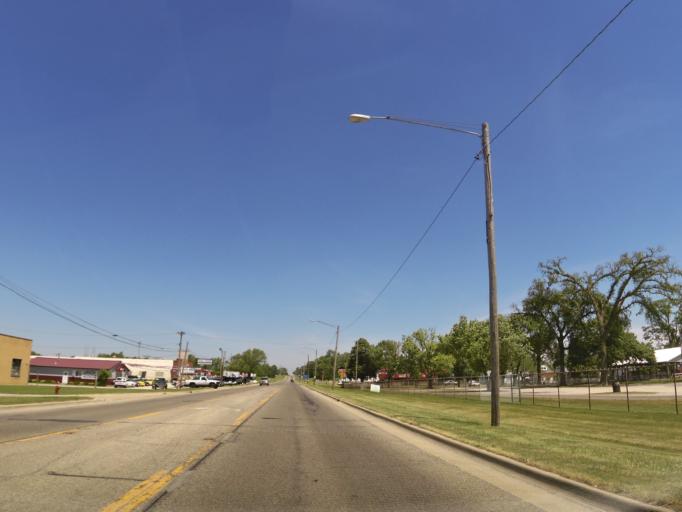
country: US
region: Illinois
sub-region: Vermilion County
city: Hoopeston
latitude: 40.4644
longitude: -87.6875
